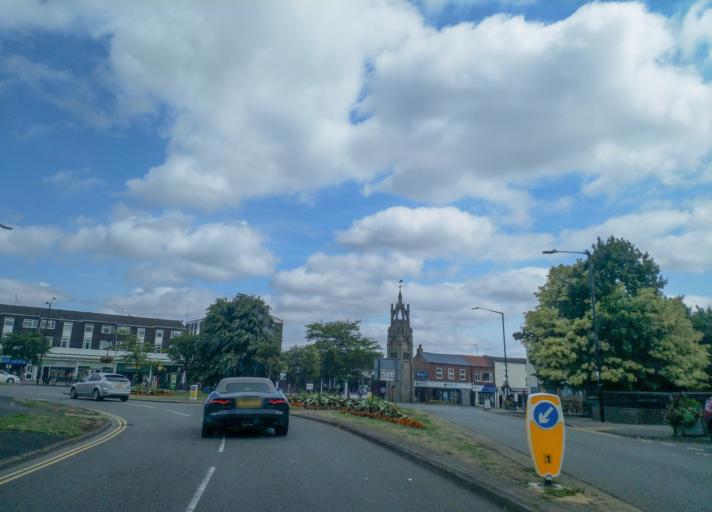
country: GB
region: England
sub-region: Warwickshire
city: Kenilworth
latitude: 52.3436
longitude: -1.5808
